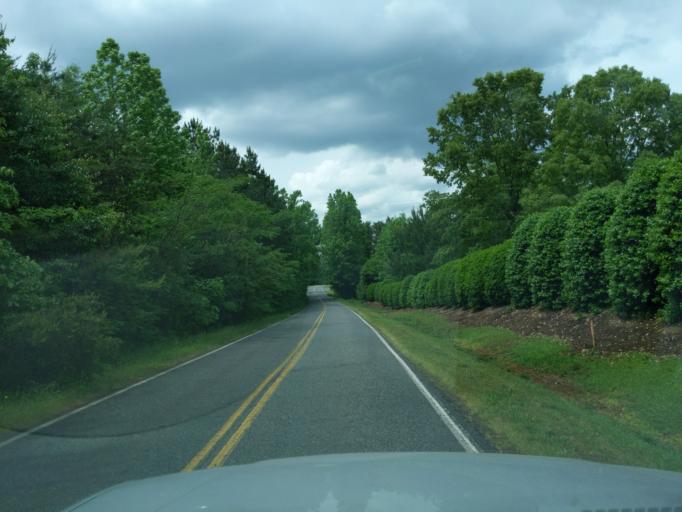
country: US
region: South Carolina
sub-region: Spartanburg County
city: Inman Mills
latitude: 35.0023
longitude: -82.1161
